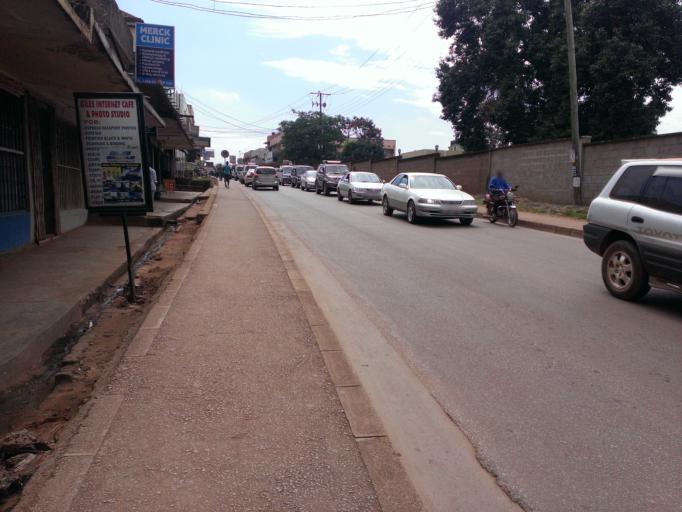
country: UG
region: Central Region
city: Kampala Central Division
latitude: 0.3103
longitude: 32.5580
